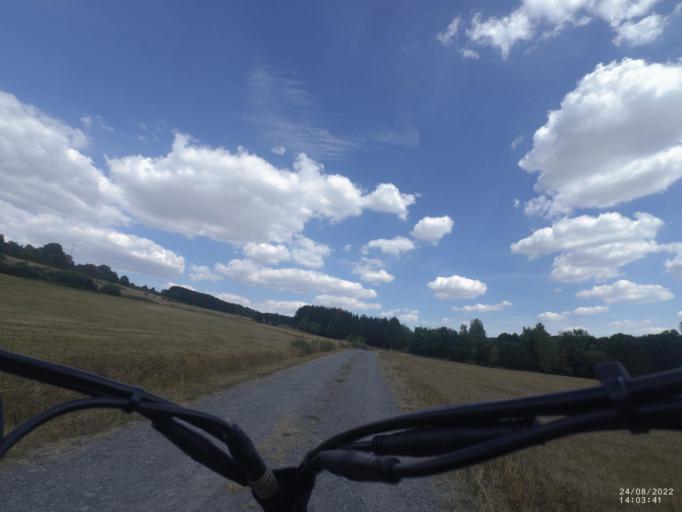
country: DE
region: Rheinland-Pfalz
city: Neroth
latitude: 50.1998
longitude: 6.7518
